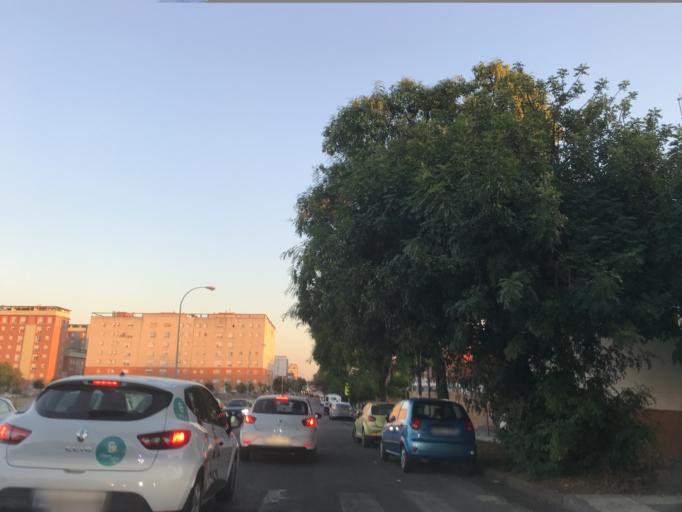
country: ES
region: Andalusia
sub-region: Provincia de Sevilla
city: Sevilla
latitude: 37.4053
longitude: -5.9232
